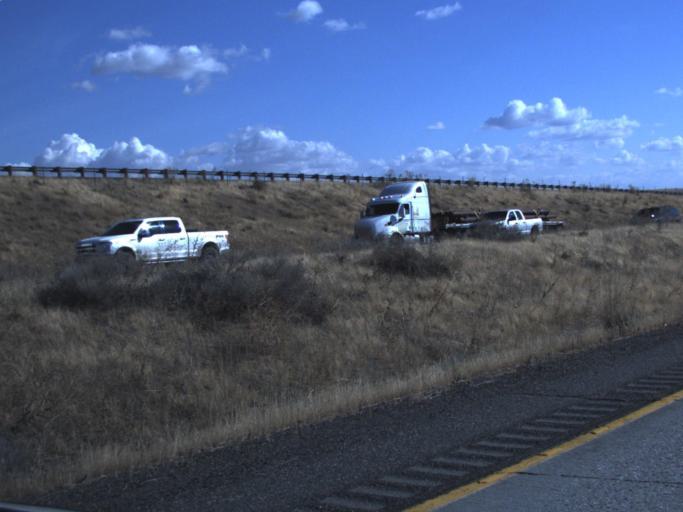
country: US
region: Washington
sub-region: Benton County
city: Highland
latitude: 46.0430
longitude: -119.2246
